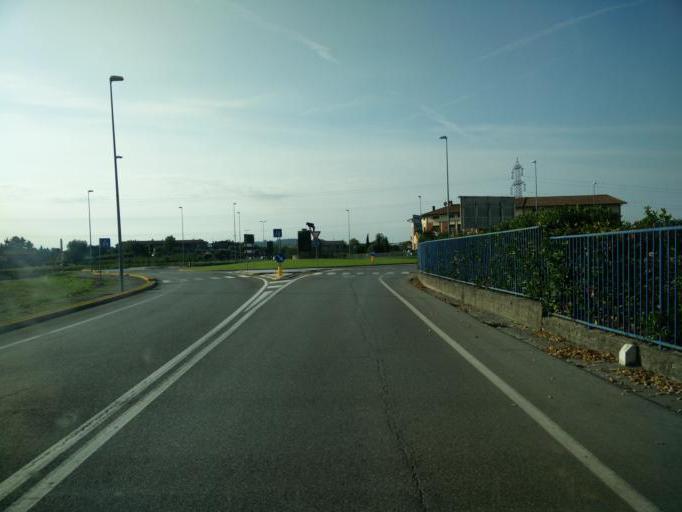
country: IT
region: Lombardy
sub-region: Provincia di Brescia
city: Corte Franca
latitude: 45.6270
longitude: 10.0073
